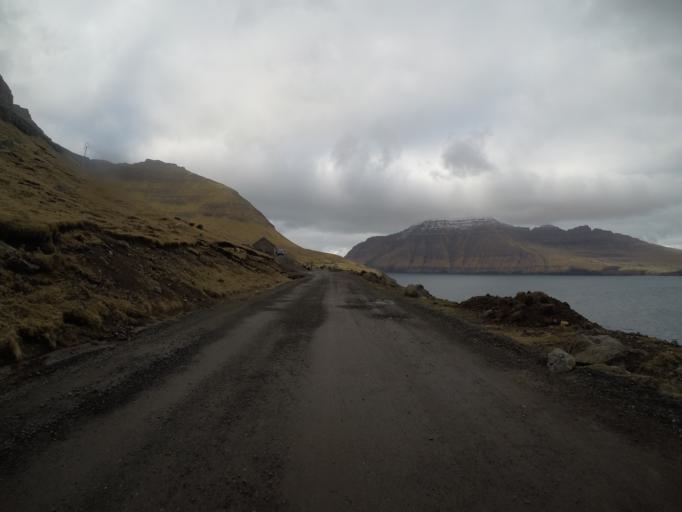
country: FO
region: Nordoyar
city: Klaksvik
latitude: 62.3460
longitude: -6.5803
